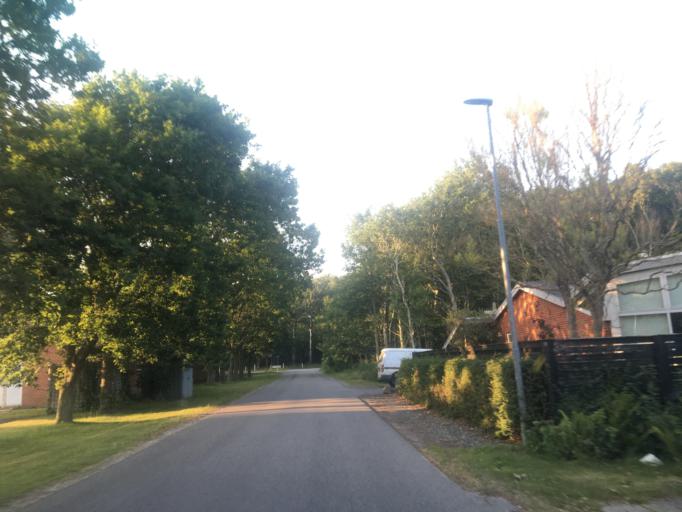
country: DK
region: North Denmark
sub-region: Thisted Kommune
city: Hurup
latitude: 56.8524
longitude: 8.3651
